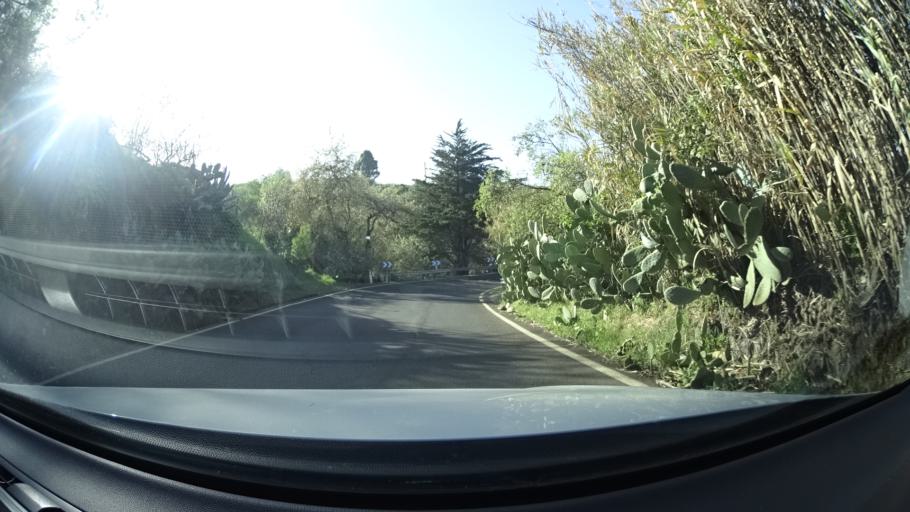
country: ES
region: Canary Islands
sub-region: Provincia de Las Palmas
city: Vega de San Mateo
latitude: 28.0164
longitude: -15.5395
